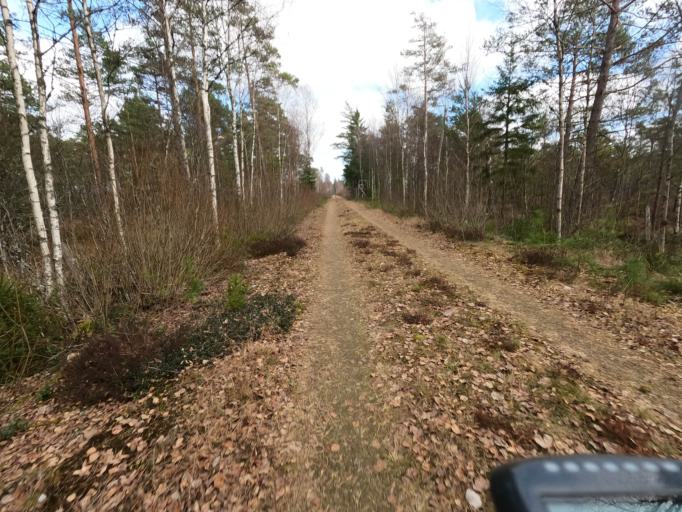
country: SE
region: Kronoberg
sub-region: Alvesta Kommun
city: Vislanda
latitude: 56.8226
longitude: 14.3050
